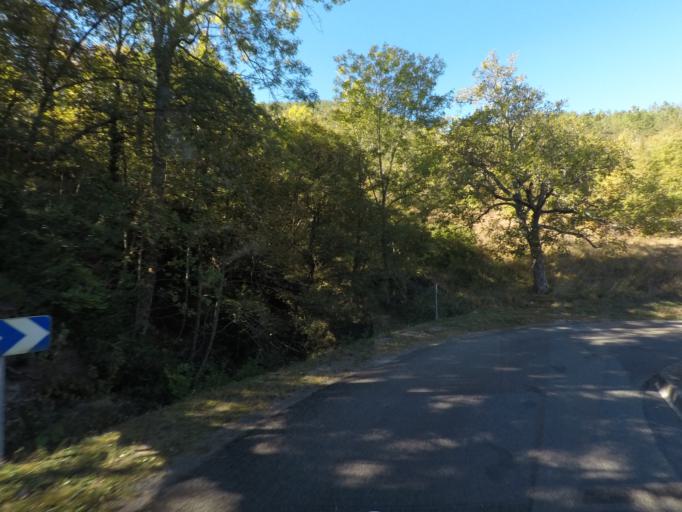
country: FR
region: Rhone-Alpes
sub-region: Departement de la Drome
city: Die
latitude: 44.5572
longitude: 5.3425
